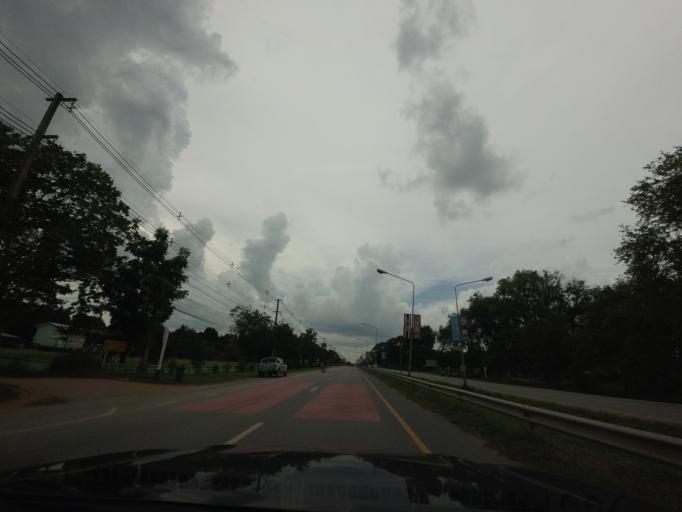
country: TH
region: Changwat Nong Bua Lamphu
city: Nong Bua Lamphu
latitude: 17.2412
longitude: 102.3912
